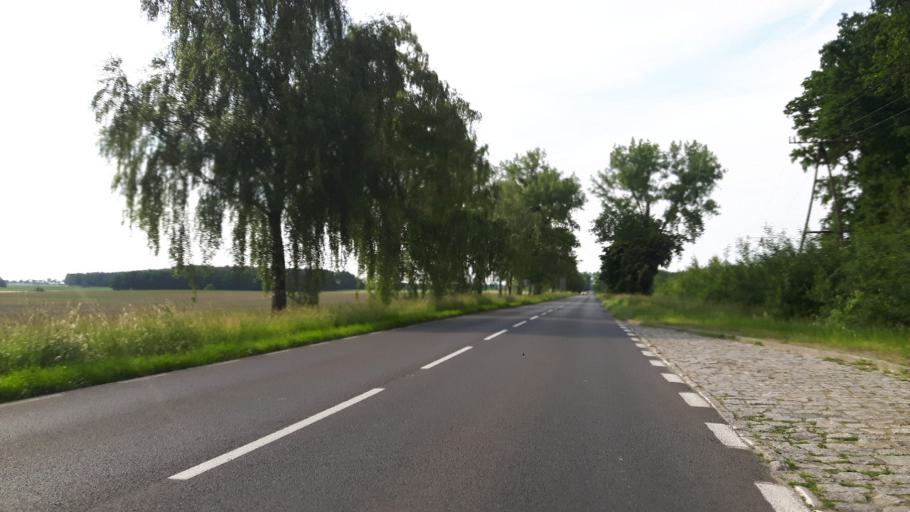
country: PL
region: West Pomeranian Voivodeship
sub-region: Powiat gryficki
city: Gryfice
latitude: 53.8870
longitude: 15.2094
